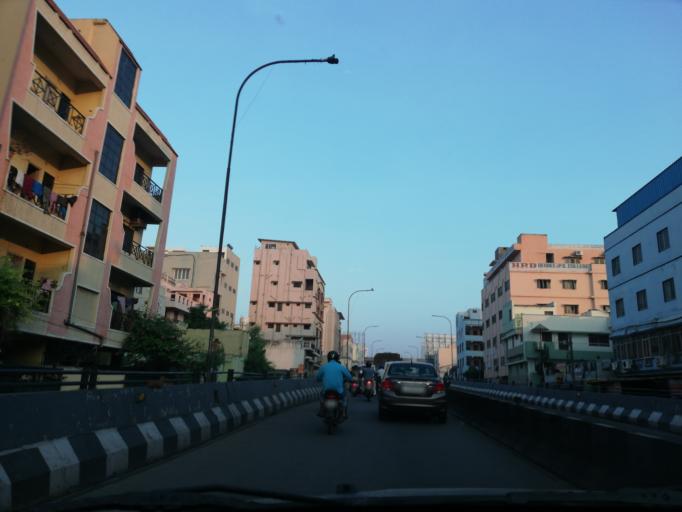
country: IN
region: Telangana
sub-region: Hyderabad
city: Hyderabad
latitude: 17.3969
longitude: 78.4956
